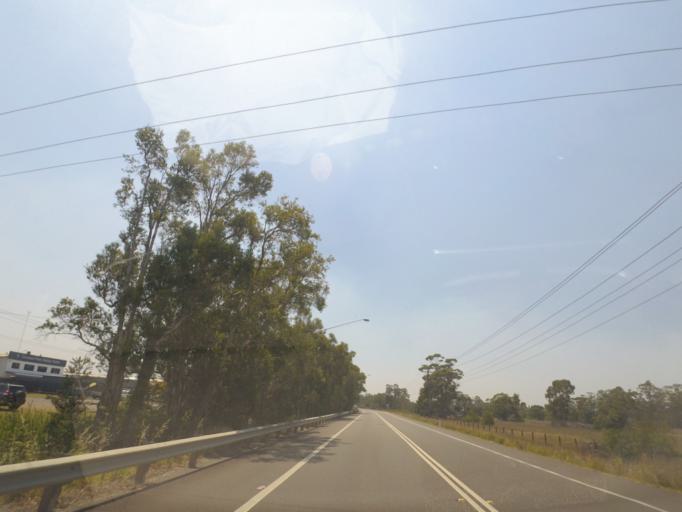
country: AU
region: New South Wales
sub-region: Newcastle
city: Mayfield West
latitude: -32.8317
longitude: 151.7278
